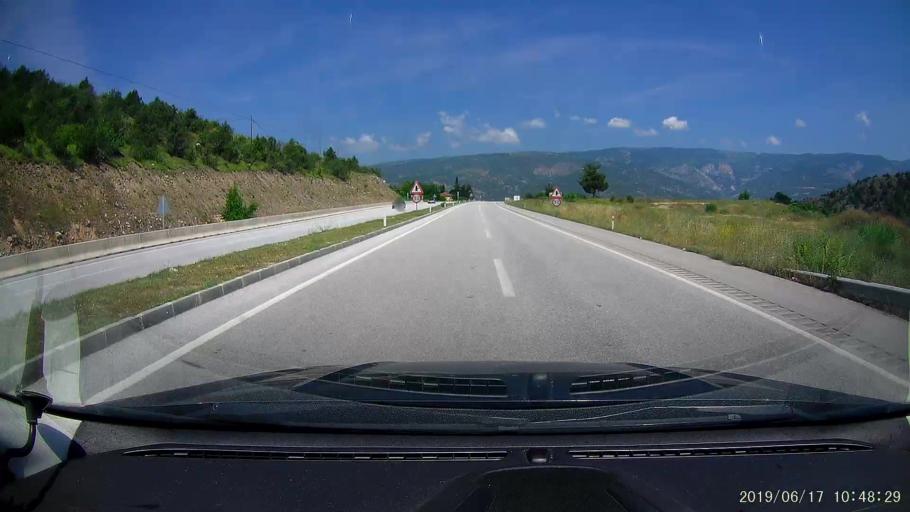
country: TR
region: Corum
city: Hacihamza
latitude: 41.0893
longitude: 34.4277
